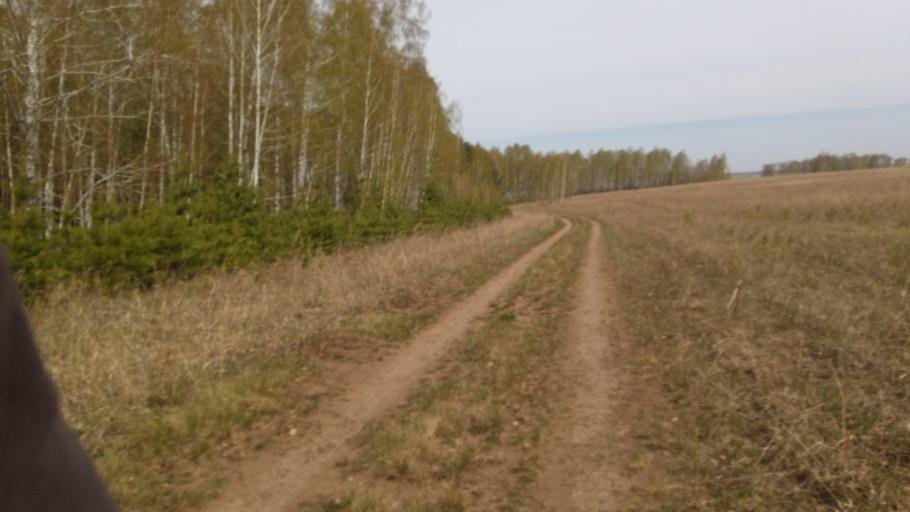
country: RU
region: Chelyabinsk
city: Timiryazevskiy
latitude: 55.0200
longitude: 60.8595
